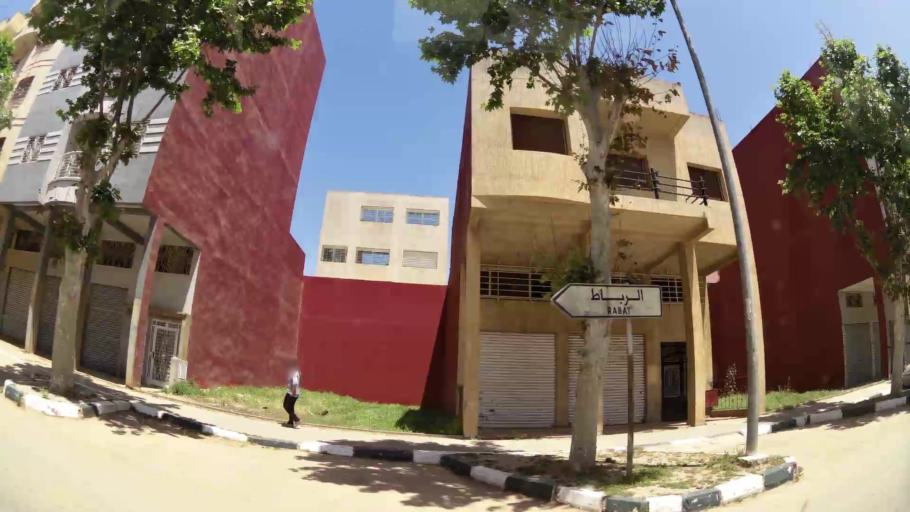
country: MA
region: Rabat-Sale-Zemmour-Zaer
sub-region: Khemisset
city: Khemisset
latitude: 33.8268
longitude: -6.0845
